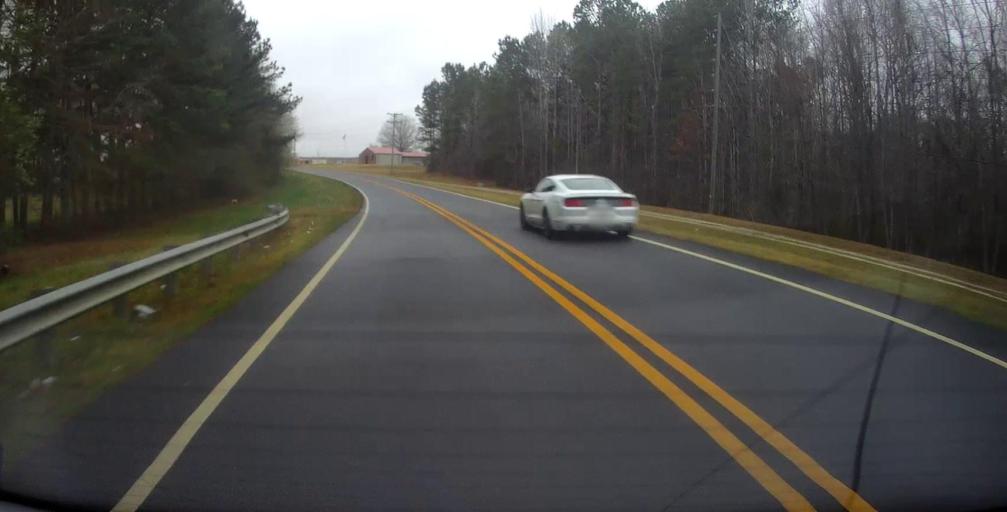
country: US
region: Georgia
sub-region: Pike County
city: Zebulon
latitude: 33.1149
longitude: -84.3559
